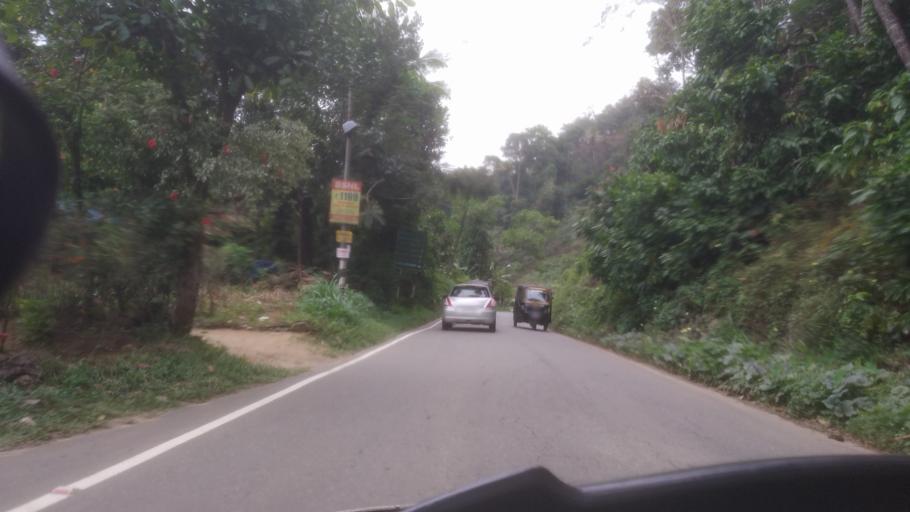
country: IN
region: Kerala
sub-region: Idukki
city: Idukki
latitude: 9.9753
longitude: 76.9975
